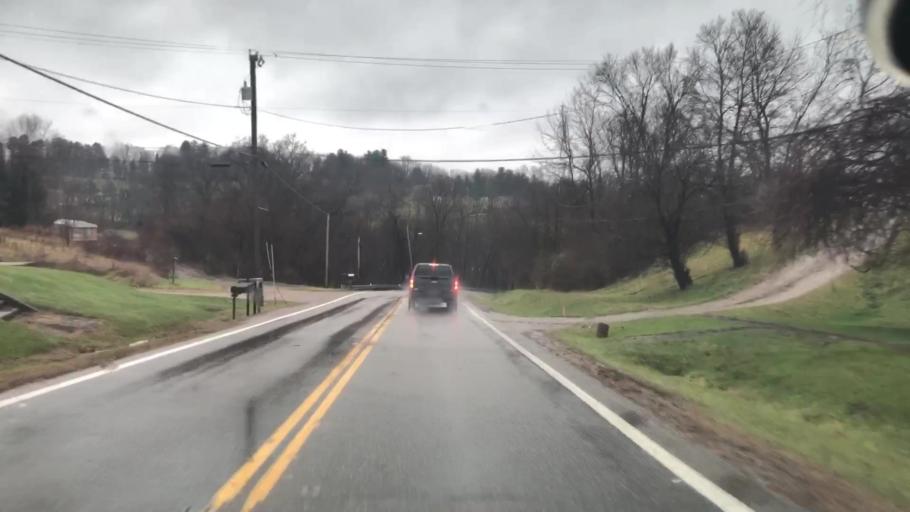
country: US
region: Ohio
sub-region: Belmont County
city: Saint Clairsville
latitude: 40.1255
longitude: -80.9403
